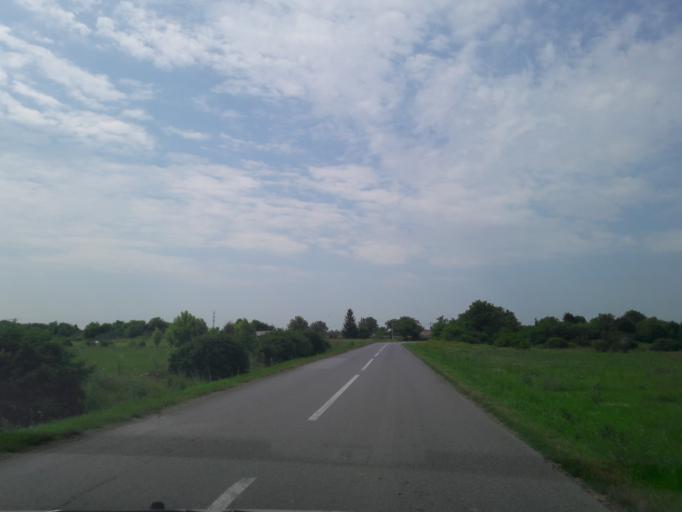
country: HR
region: Osjecko-Baranjska
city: Bizovac
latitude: 45.5044
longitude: 18.4509
